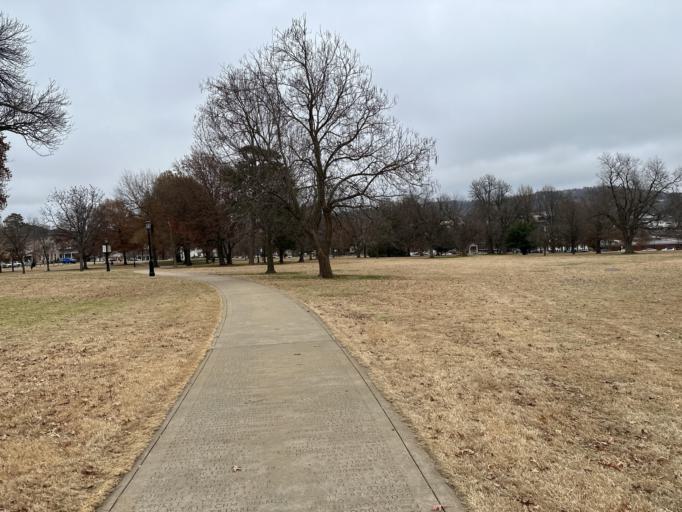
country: US
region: Arkansas
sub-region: Washington County
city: Fayetteville
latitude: 36.0682
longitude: -94.1707
